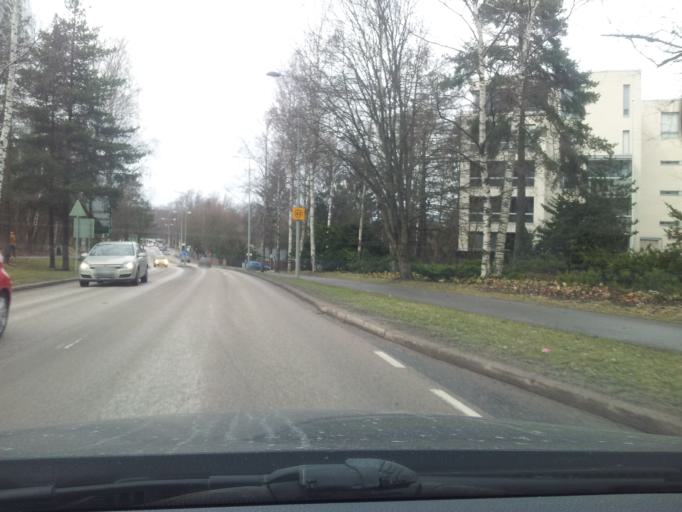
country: FI
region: Uusimaa
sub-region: Helsinki
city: Otaniemi
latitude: 60.1794
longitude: 24.7982
